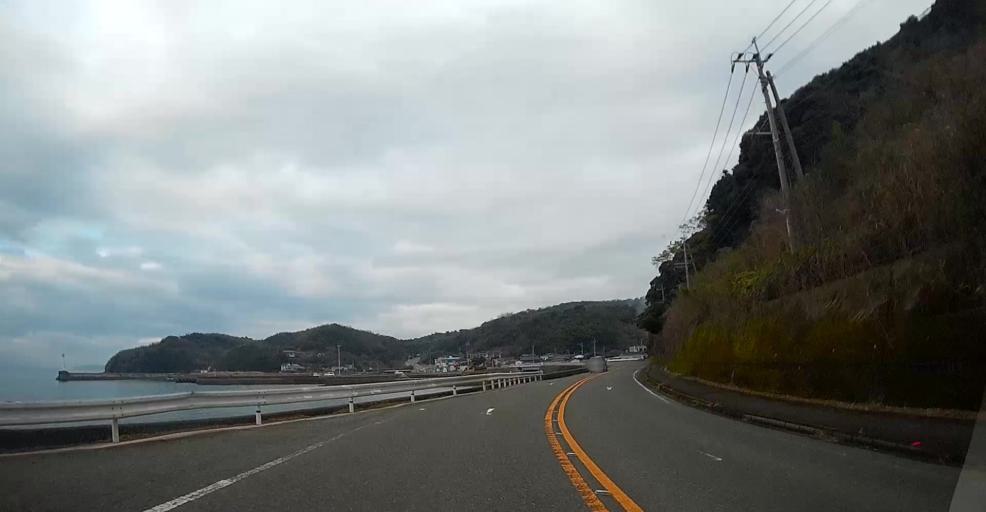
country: JP
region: Kumamoto
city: Hondo
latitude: 32.4901
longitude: 130.2910
